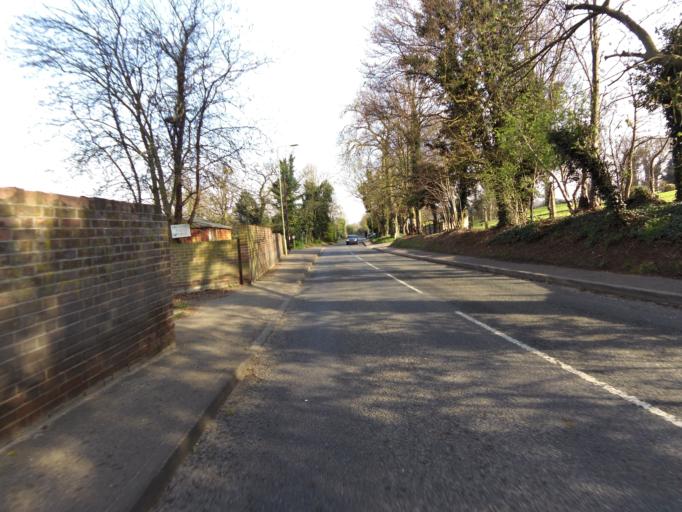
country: GB
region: England
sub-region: Suffolk
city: Bramford
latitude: 52.0728
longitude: 1.1075
